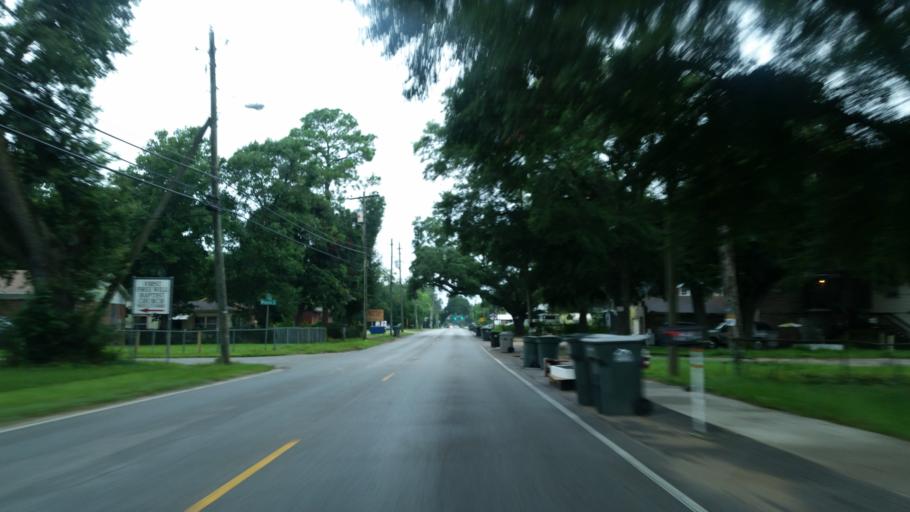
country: US
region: Florida
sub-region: Escambia County
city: West Pensacola
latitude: 30.4188
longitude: -87.2686
